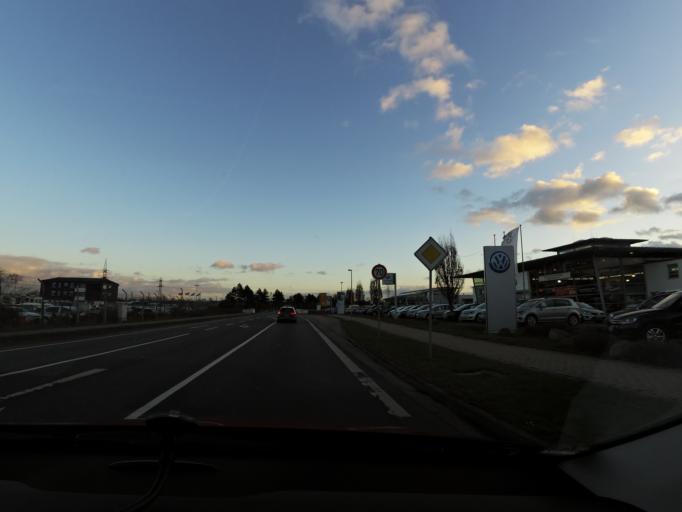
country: DE
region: Lower Saxony
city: Lehrte
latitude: 52.3959
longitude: 9.9740
